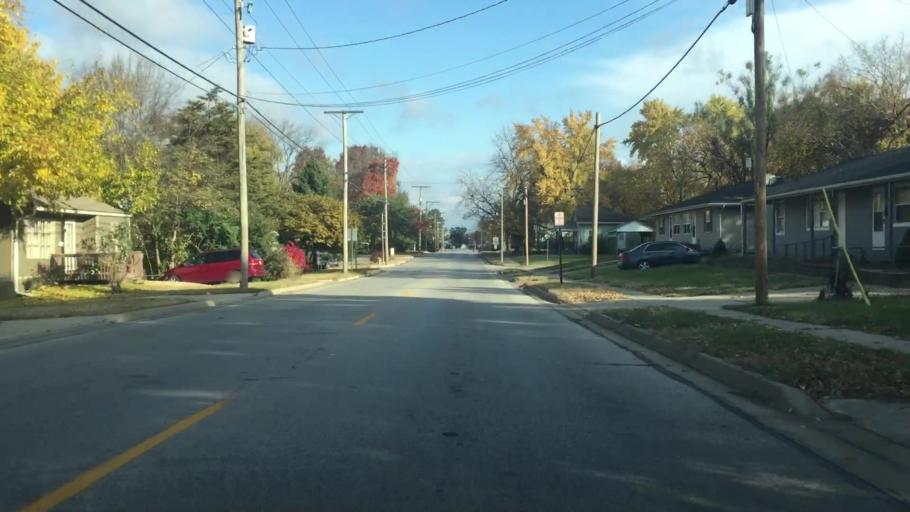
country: US
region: Missouri
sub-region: Jackson County
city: Grandview
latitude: 38.8848
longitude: -94.5398
